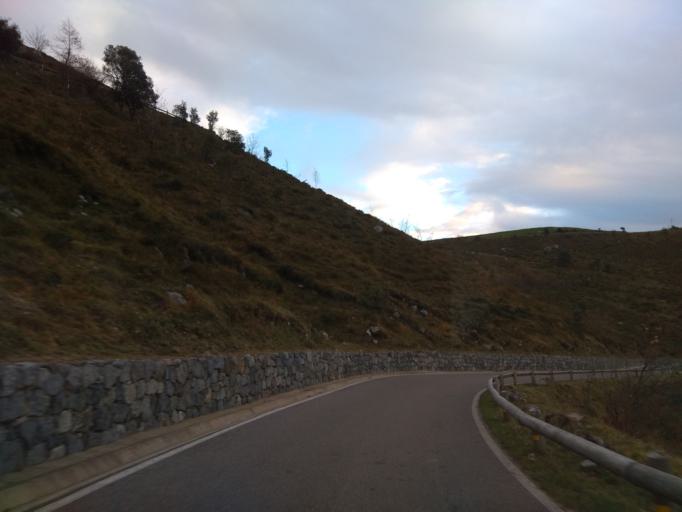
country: ES
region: Cantabria
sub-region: Provincia de Cantabria
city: Arredondo
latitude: 43.2053
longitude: -3.5837
